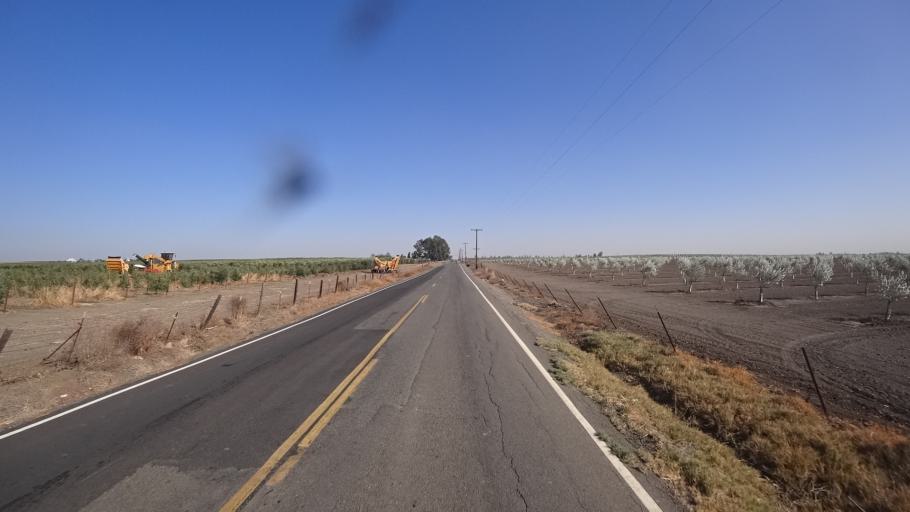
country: US
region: California
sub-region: Yolo County
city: Cottonwood
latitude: 38.7135
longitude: -121.9150
